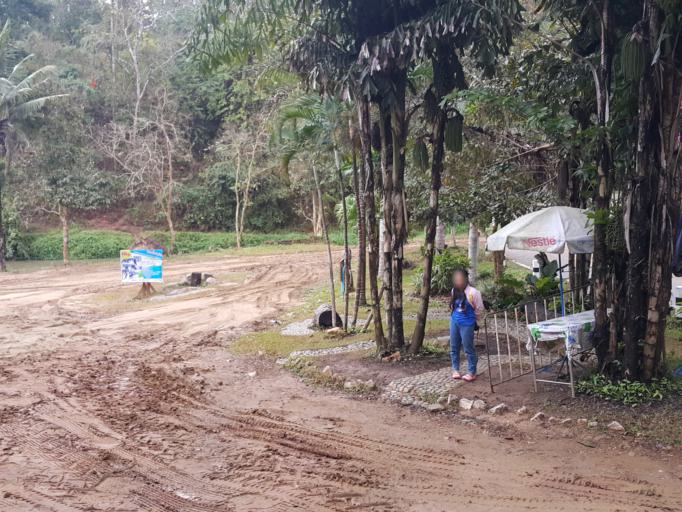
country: TH
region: Lampang
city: Hang Chat
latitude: 18.3593
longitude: 99.2489
